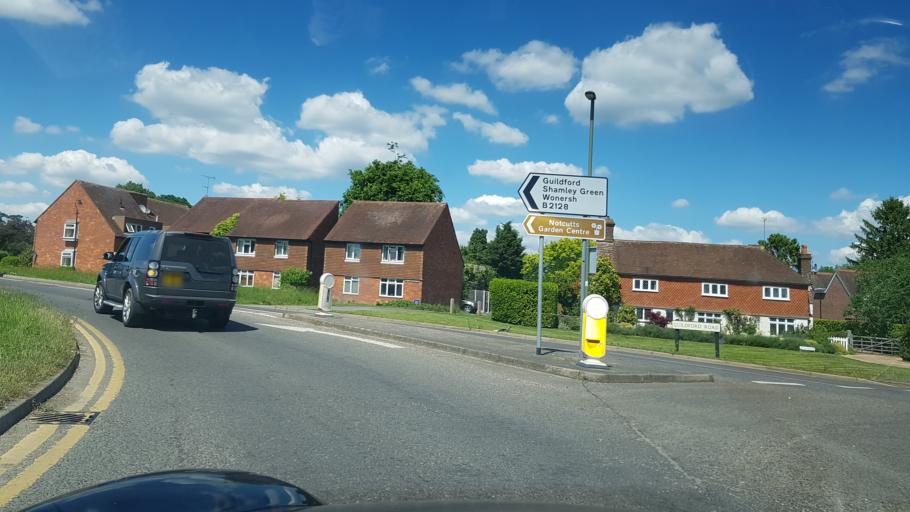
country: GB
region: England
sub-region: Surrey
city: Cranleigh
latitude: 51.1446
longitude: -0.5008
